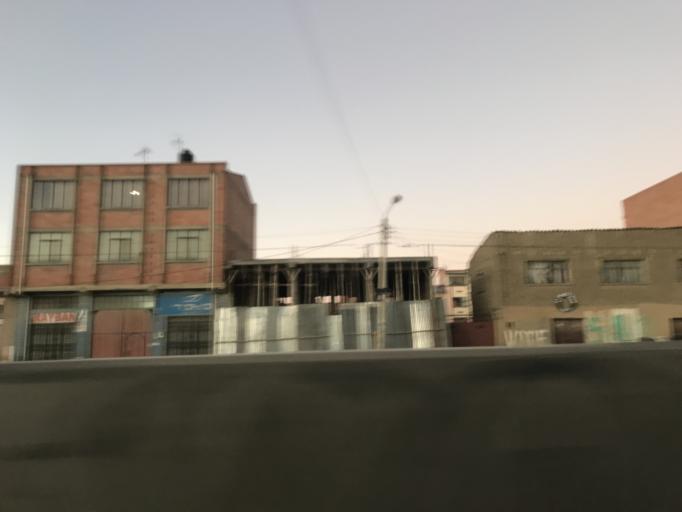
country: BO
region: La Paz
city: La Paz
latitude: -16.4865
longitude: -68.2243
